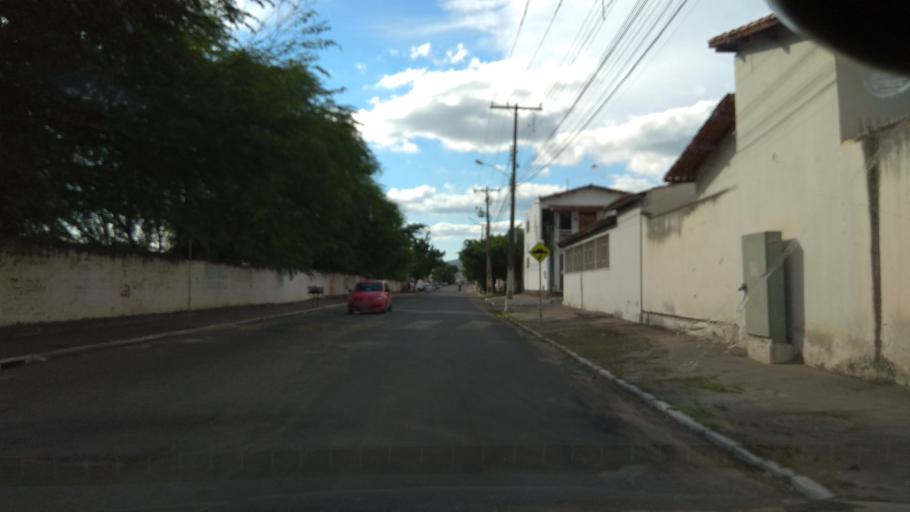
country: BR
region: Bahia
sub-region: Jequie
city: Jequie
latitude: -13.8723
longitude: -40.0753
